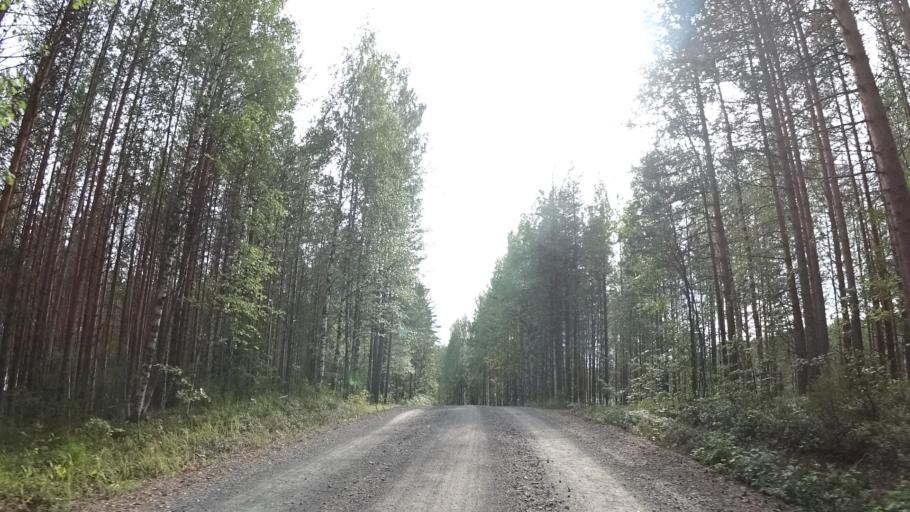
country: FI
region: North Karelia
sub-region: Joensuu
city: Ilomantsi
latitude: 62.6115
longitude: 31.1877
